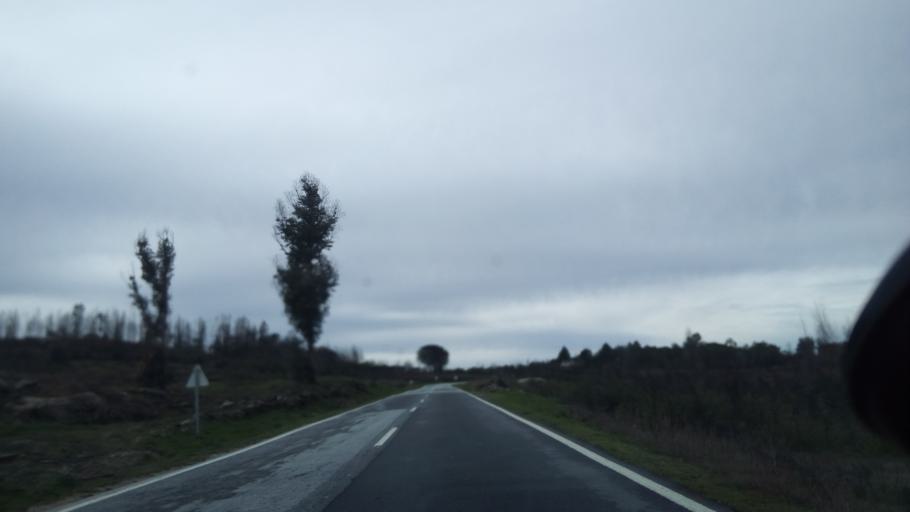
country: PT
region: Guarda
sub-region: Fornos de Algodres
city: Fornos de Algodres
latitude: 40.5246
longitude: -7.5934
